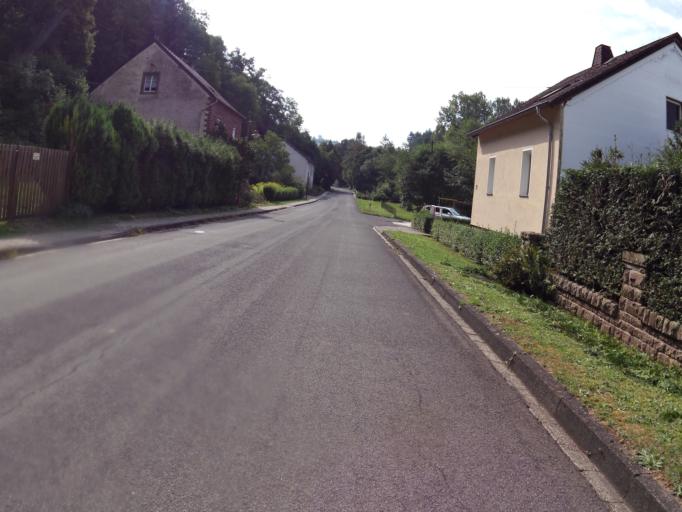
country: DE
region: Rheinland-Pfalz
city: Philippsheim
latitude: 49.9522
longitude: 6.6290
